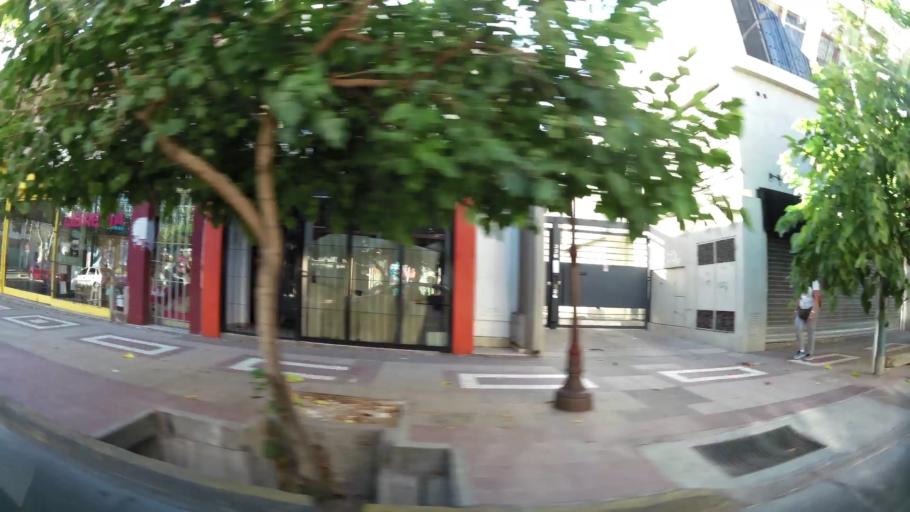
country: AR
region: Mendoza
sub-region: Departamento de Godoy Cruz
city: Godoy Cruz
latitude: -32.9287
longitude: -68.8447
